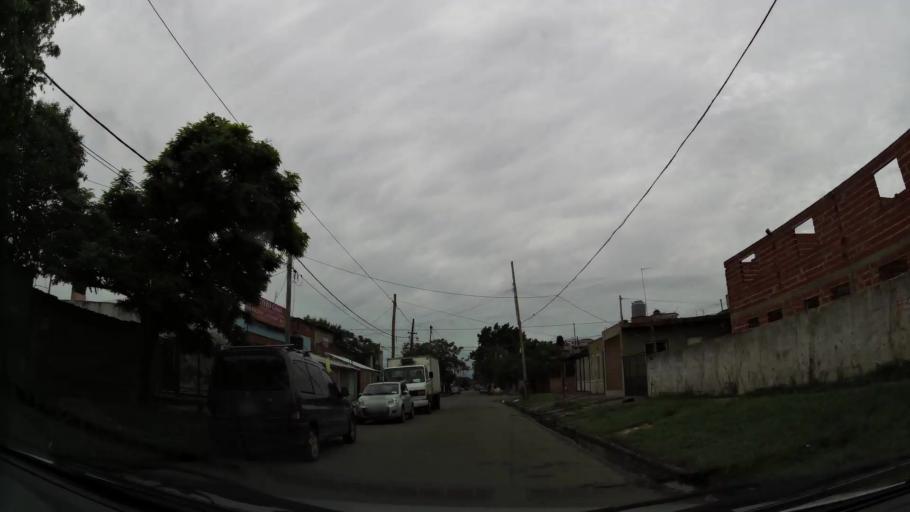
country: AR
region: Buenos Aires
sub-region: Partido de Lomas de Zamora
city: Lomas de Zamora
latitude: -34.7417
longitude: -58.3617
